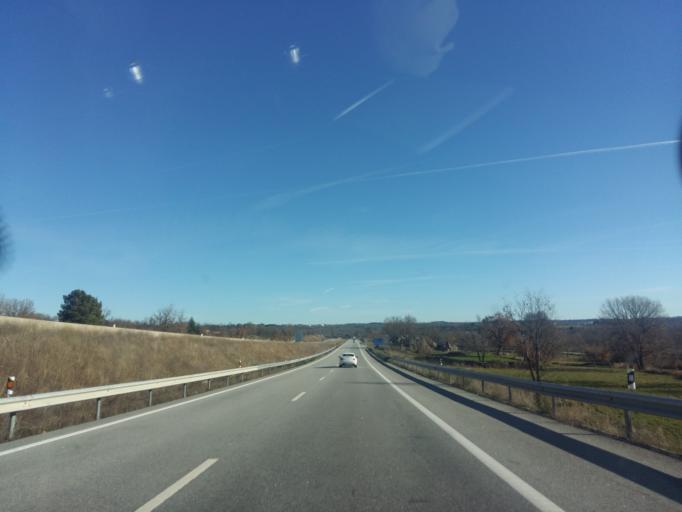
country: PT
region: Guarda
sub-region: Pinhel
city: Pinhel
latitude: 40.6039
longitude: -7.0568
